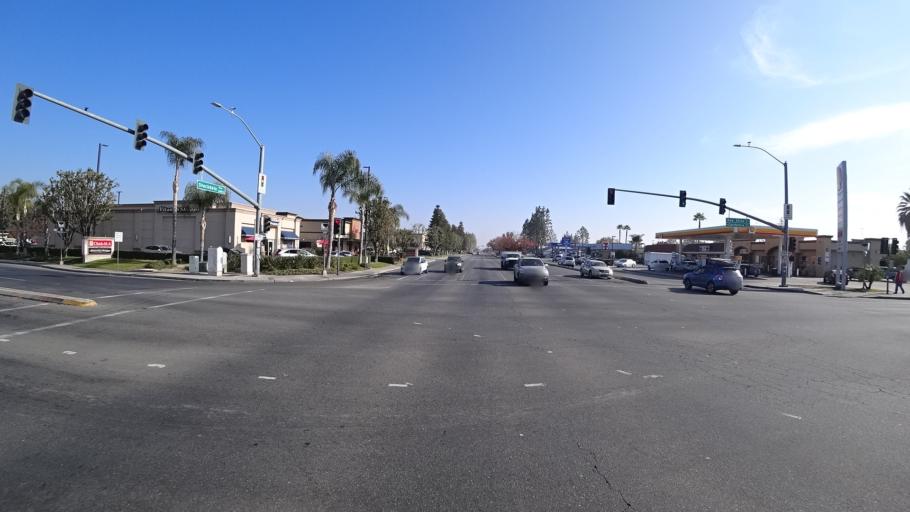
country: US
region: California
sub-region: Kern County
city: Bakersfield
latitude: 35.3543
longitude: -119.0612
